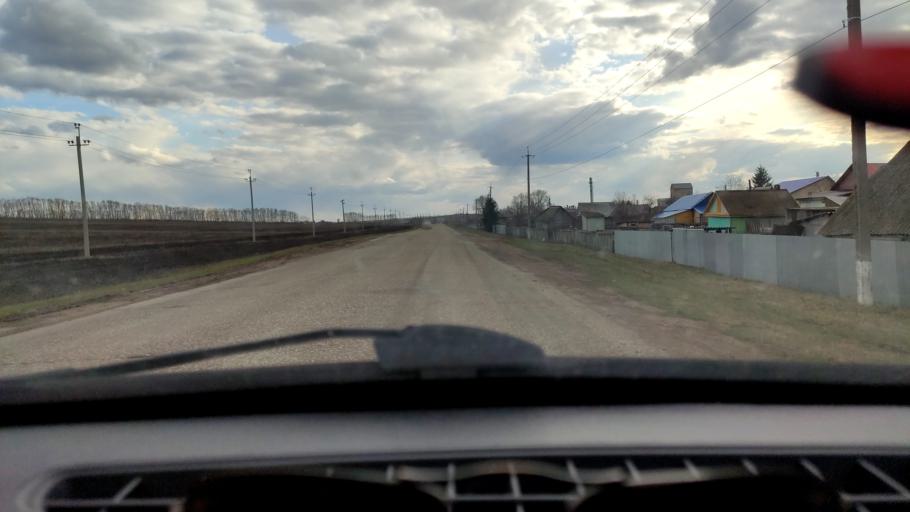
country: RU
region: Bashkortostan
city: Karmaskaly
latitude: 54.3988
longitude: 56.2478
